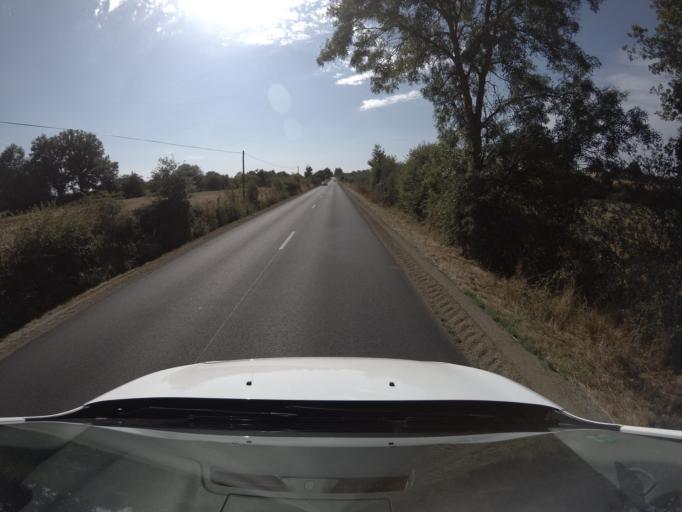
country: FR
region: Poitou-Charentes
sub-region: Departement des Deux-Sevres
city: Mauze-Thouarsais
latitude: 46.9991
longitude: -0.3113
